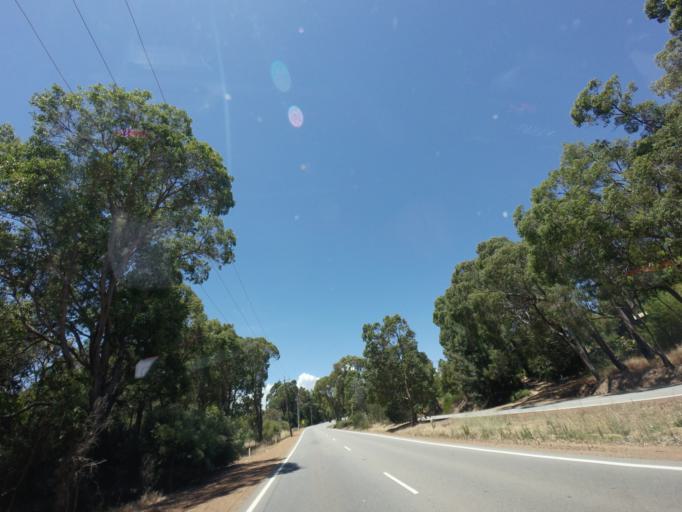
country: AU
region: Western Australia
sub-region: Mundaring
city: Parkerville
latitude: -31.8995
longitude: 116.1376
